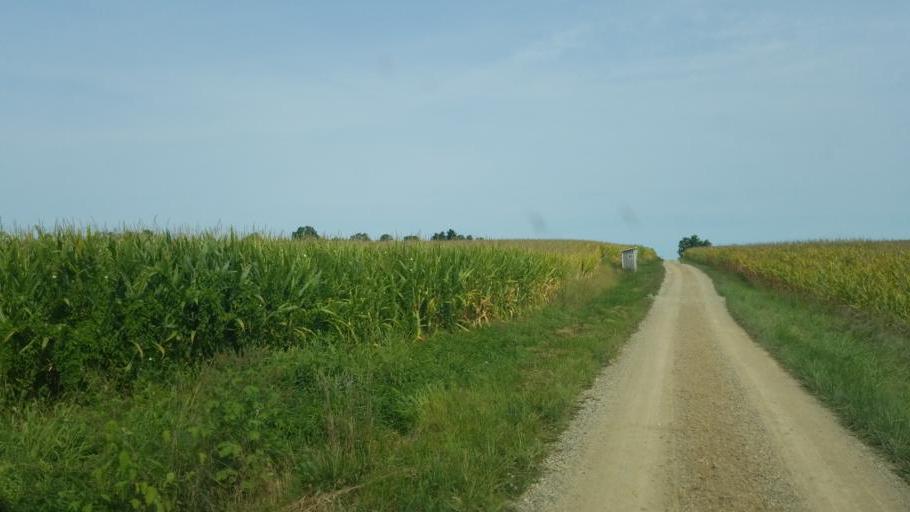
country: US
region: Ohio
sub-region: Knox County
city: Fredericktown
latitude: 40.4968
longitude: -82.5964
